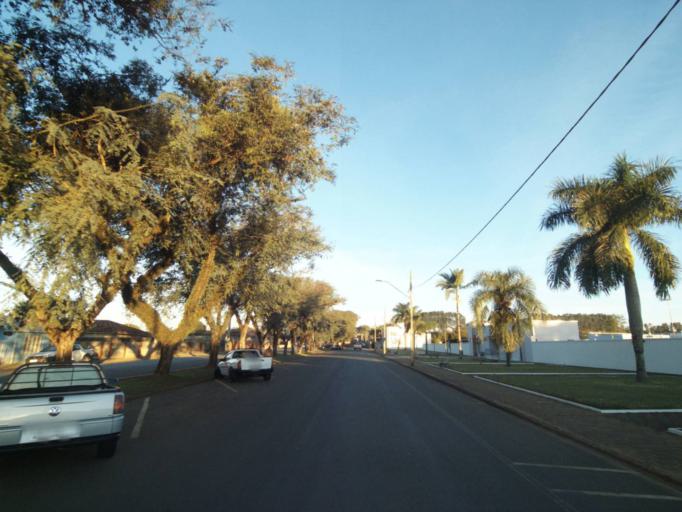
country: BR
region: Parana
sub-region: Tibagi
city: Tibagi
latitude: -24.5157
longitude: -50.4150
